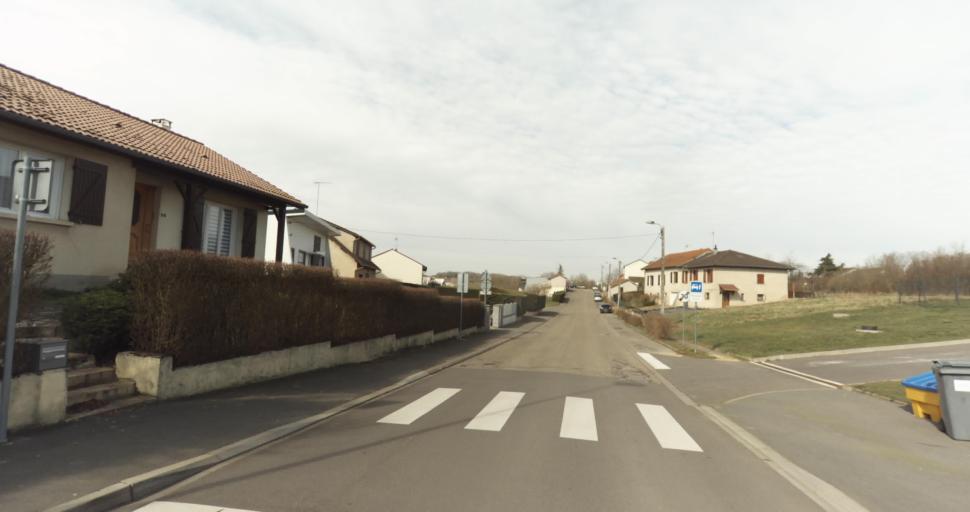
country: FR
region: Lorraine
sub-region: Departement de Meurthe-et-Moselle
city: Jarny
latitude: 49.1595
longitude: 5.8691
